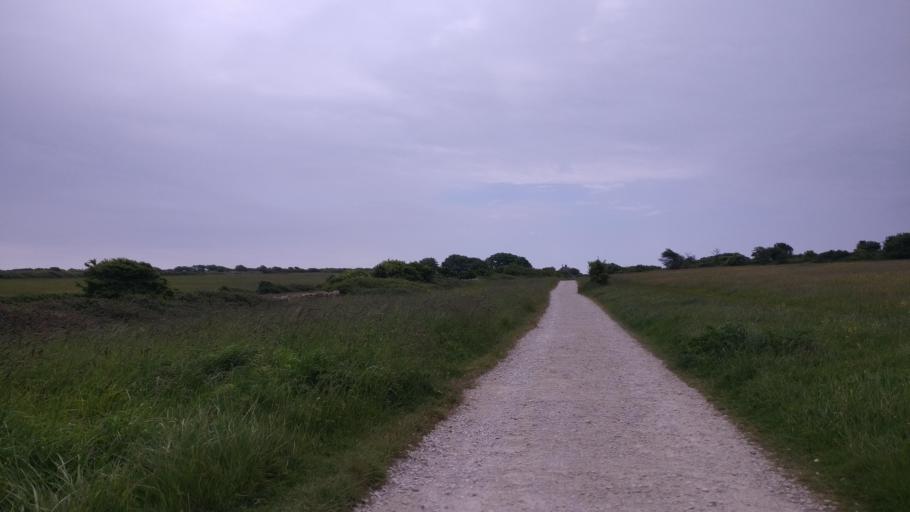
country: GB
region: England
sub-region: Dorset
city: Swanage
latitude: 50.6031
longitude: -2.0043
